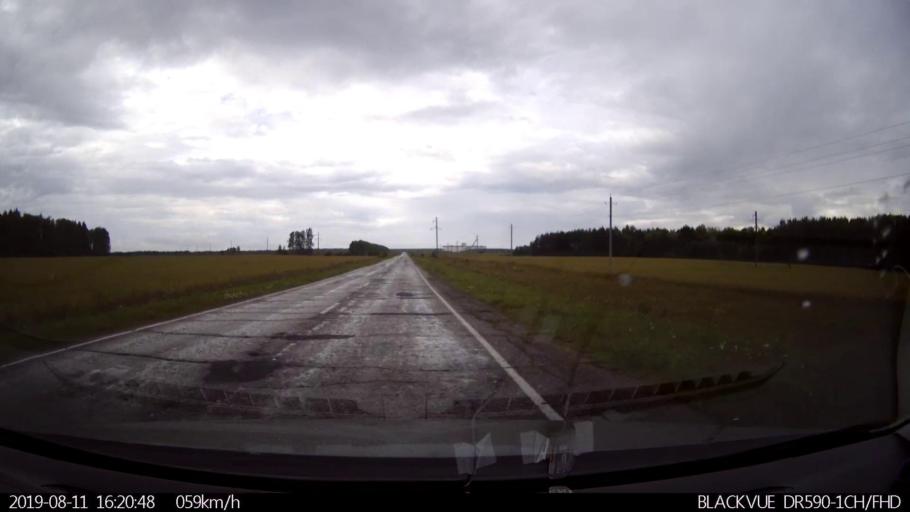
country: RU
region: Ulyanovsk
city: Mayna
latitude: 54.0748
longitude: 47.6011
